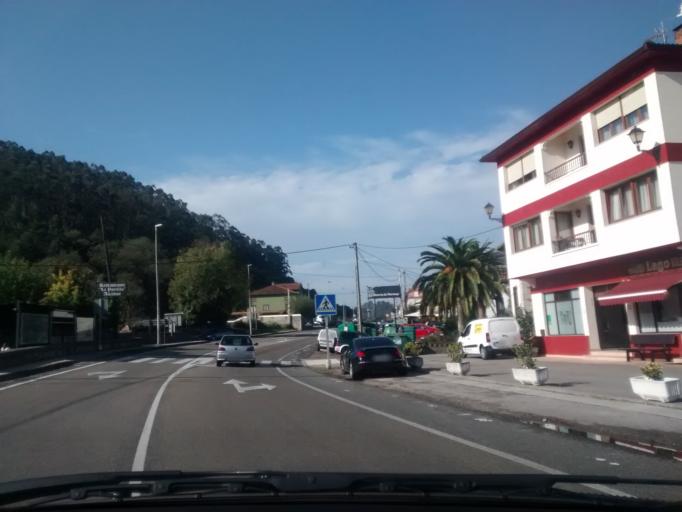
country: ES
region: Cantabria
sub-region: Provincia de Cantabria
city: Entrambasaguas
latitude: 43.3897
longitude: -3.7002
